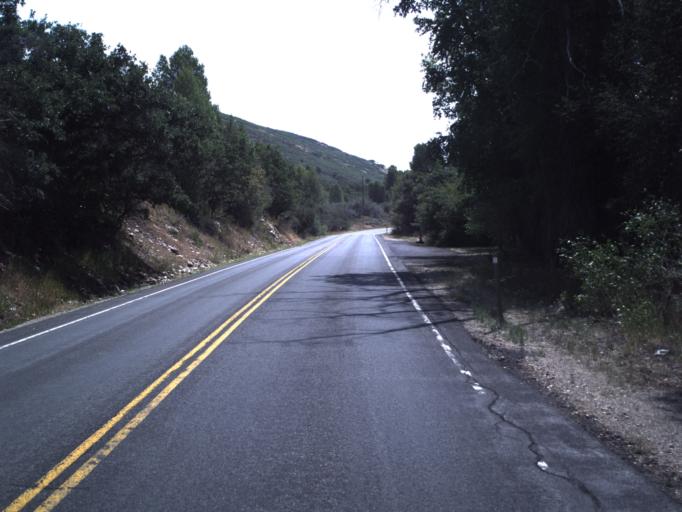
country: US
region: Utah
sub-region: Summit County
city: Francis
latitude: 40.5766
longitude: -111.2135
